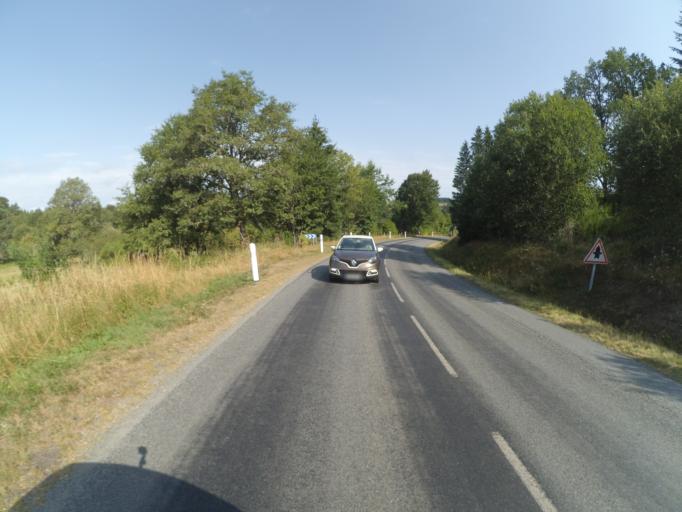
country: FR
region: Limousin
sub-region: Departement de la Correze
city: Meymac
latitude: 45.6367
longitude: 2.0984
